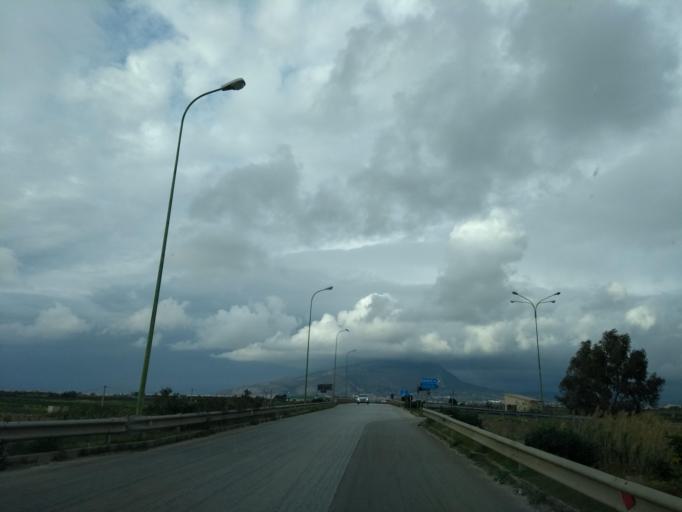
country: IT
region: Sicily
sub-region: Trapani
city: Marausa
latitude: 37.9682
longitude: 12.5212
